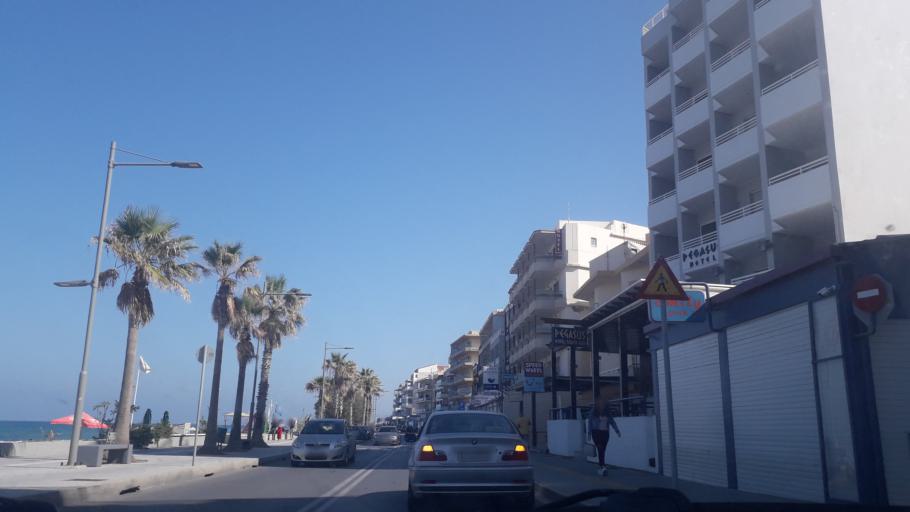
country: GR
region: Crete
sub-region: Nomos Rethymnis
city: Rethymno
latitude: 35.3666
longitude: 24.4873
